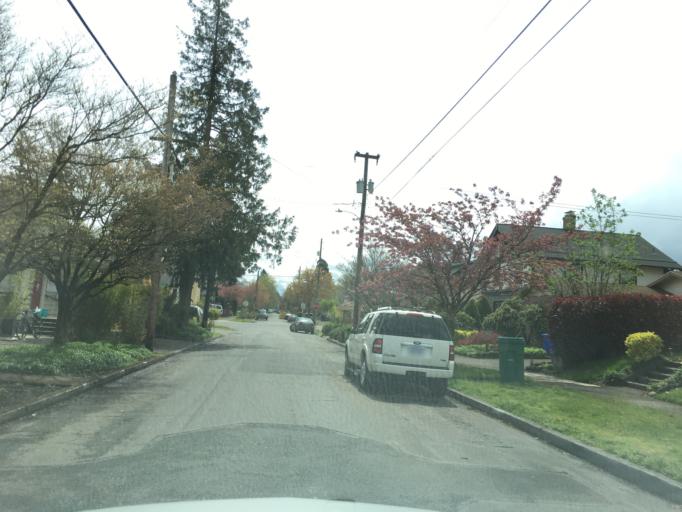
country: US
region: Oregon
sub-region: Multnomah County
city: Lents
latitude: 45.5454
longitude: -122.5984
